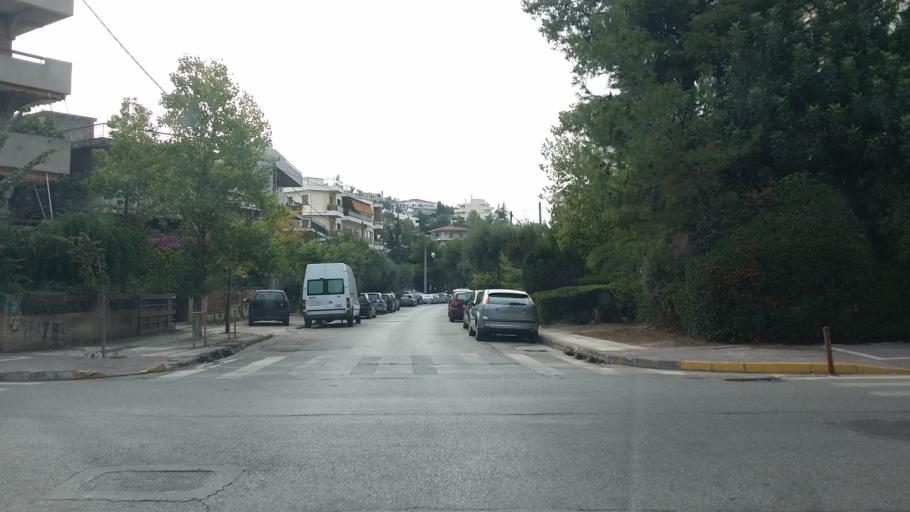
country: GR
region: Attica
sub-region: Nomarchia Athinas
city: Filothei
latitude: 38.0324
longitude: 23.7772
